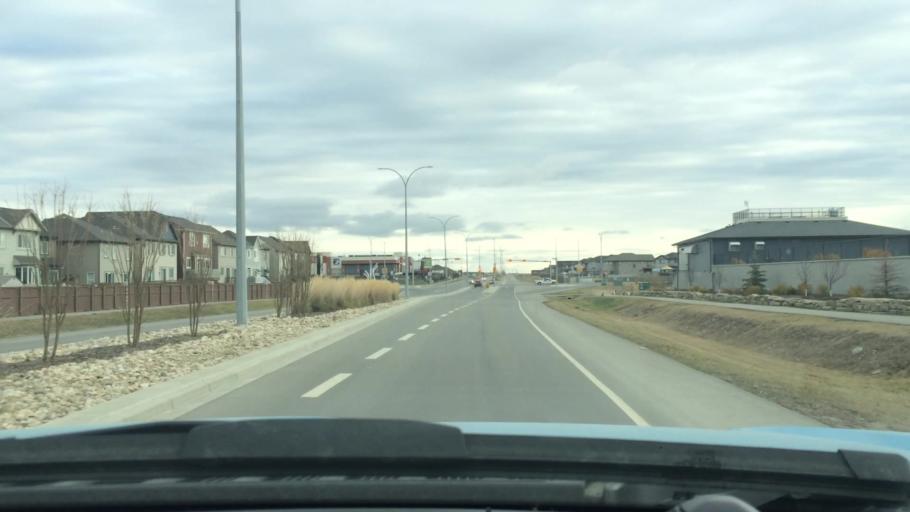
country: CA
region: Alberta
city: Airdrie
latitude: 51.2562
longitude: -114.0284
